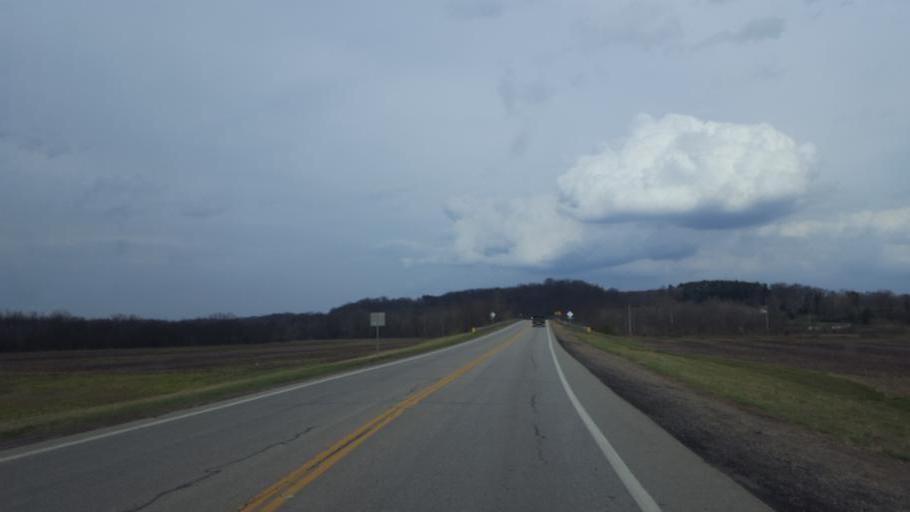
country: US
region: Ohio
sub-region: Coshocton County
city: Coshocton
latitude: 40.2368
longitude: -81.8687
